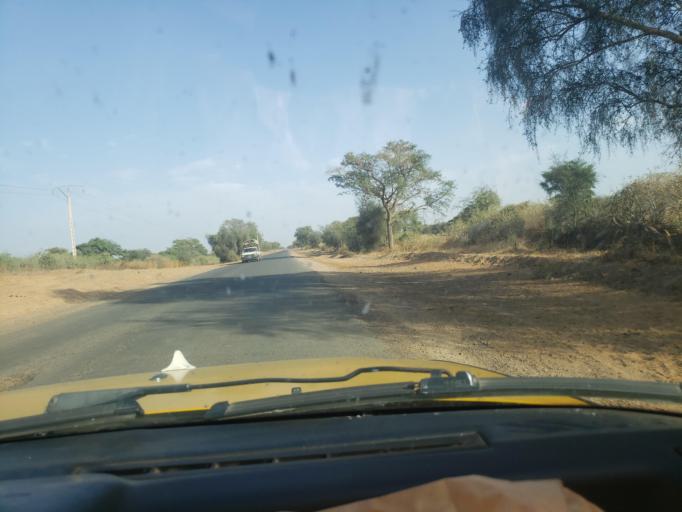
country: SN
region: Louga
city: Louga
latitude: 15.5086
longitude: -15.9747
